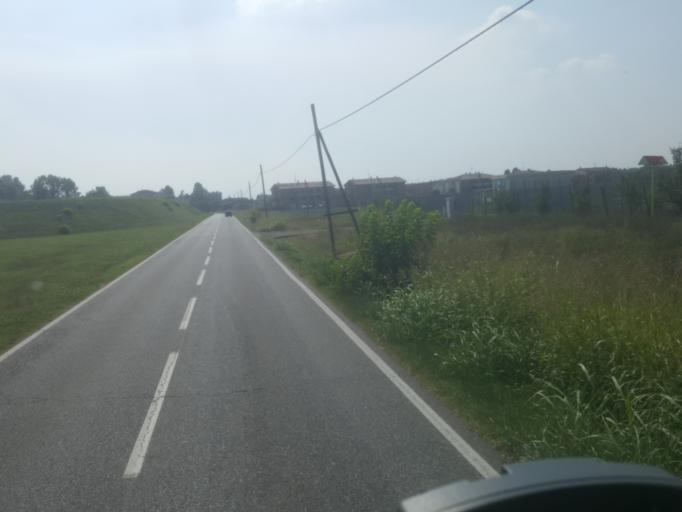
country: IT
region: Emilia-Romagna
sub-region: Provincia di Parma
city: Torrile
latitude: 44.9243
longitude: 10.3321
